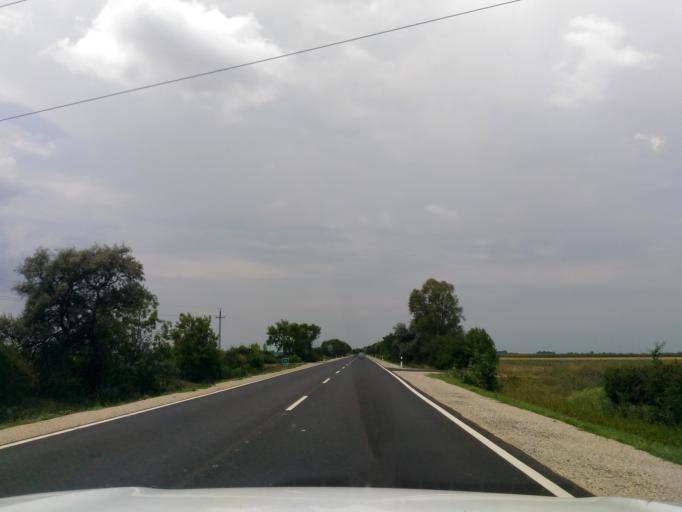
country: HU
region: Jasz-Nagykun-Szolnok
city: Szolnok
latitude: 47.1806
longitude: 20.1229
